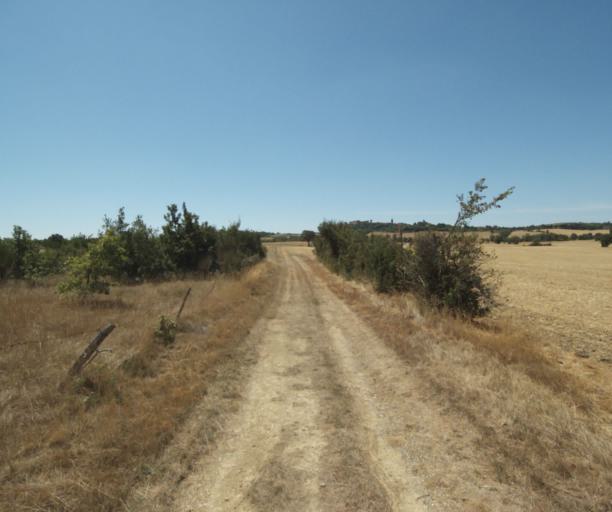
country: FR
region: Midi-Pyrenees
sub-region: Departement de la Haute-Garonne
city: Saint-Felix-Lauragais
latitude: 43.4537
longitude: 1.9057
